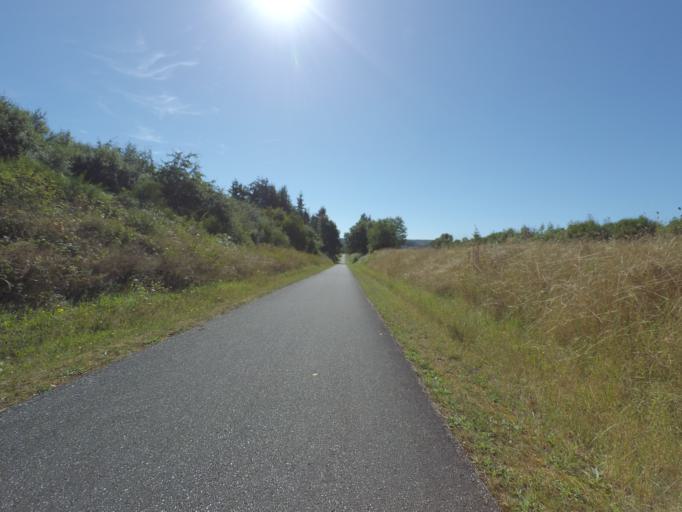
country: DE
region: Rheinland-Pfalz
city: Hasborn
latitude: 50.0619
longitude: 6.9063
